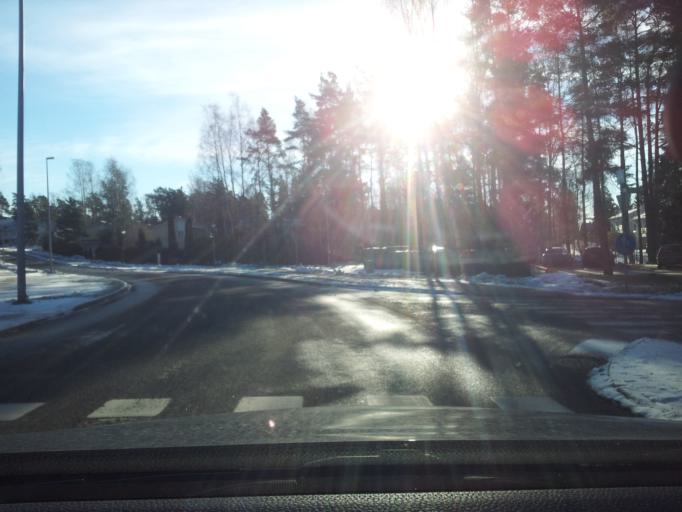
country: FI
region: Uusimaa
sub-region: Helsinki
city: Koukkuniemi
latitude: 60.1488
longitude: 24.7387
